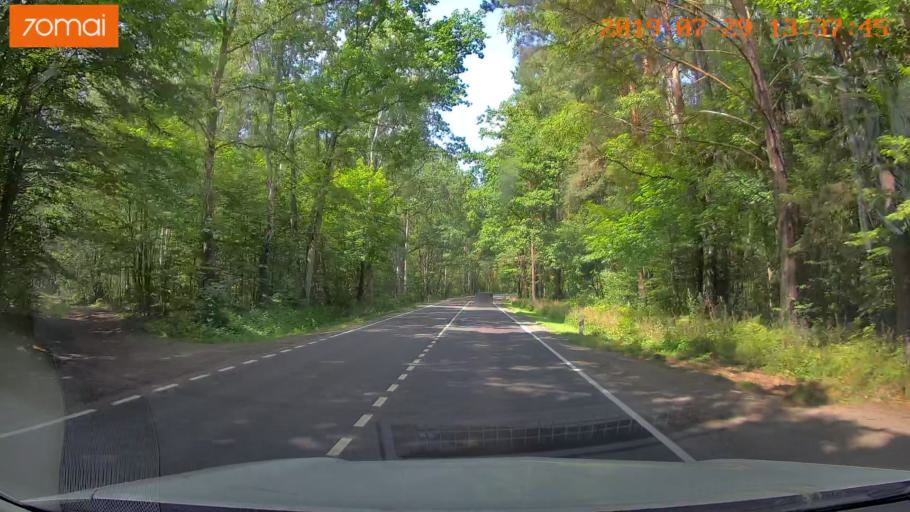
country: RU
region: Kaliningrad
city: Volochayevskoye
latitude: 54.7162
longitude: 20.1799
